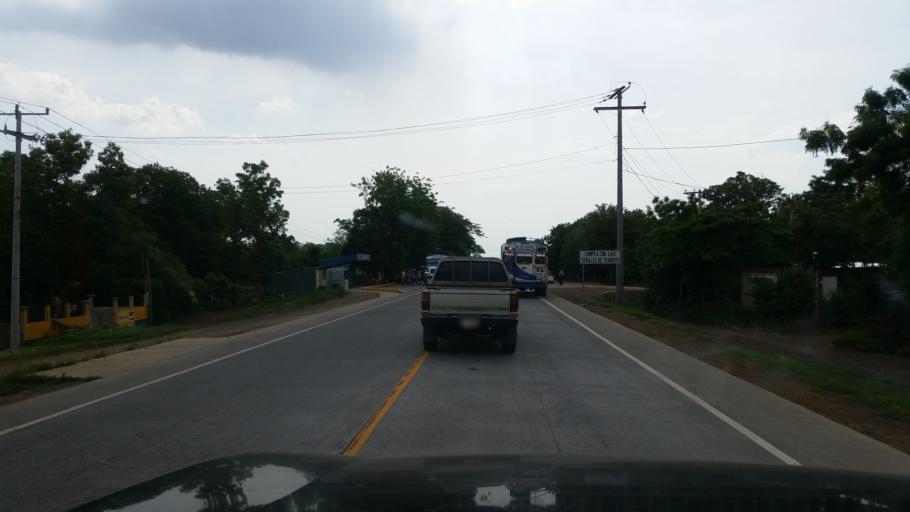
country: NI
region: Managua
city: Carlos Fonseca Amador
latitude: 12.0647
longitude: -86.4719
